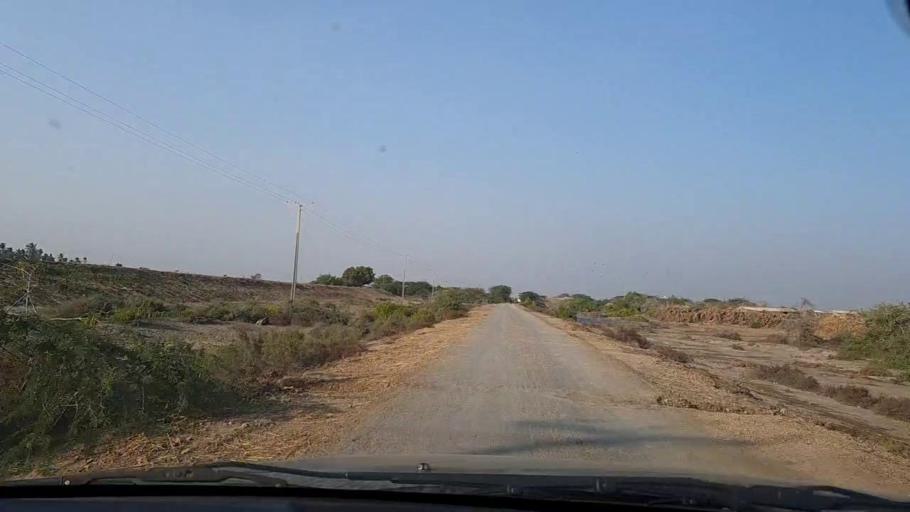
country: PK
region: Sindh
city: Chuhar Jamali
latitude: 24.2966
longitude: 67.7551
